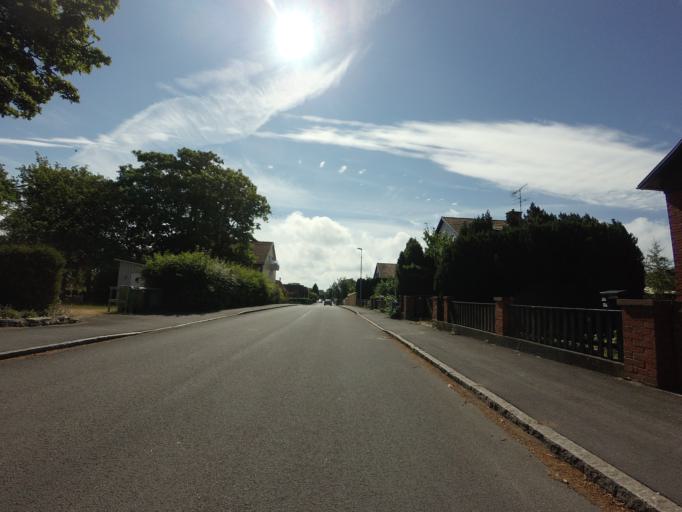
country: SE
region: Skane
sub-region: Simrishamns Kommun
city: Simrishamn
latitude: 55.4729
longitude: 14.2791
